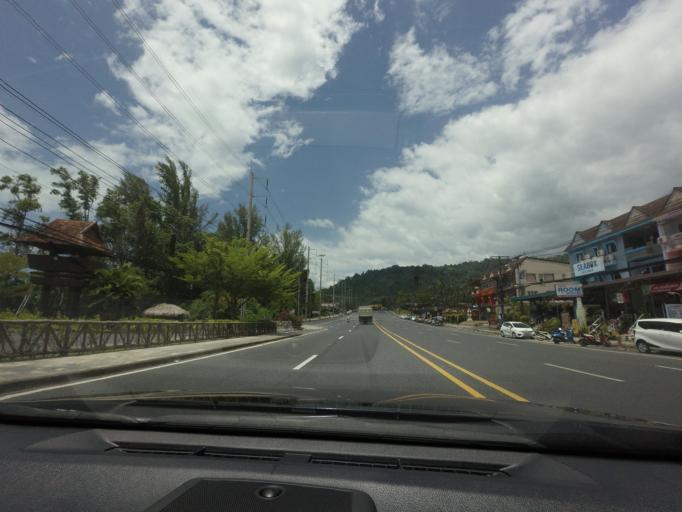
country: TH
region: Phangnga
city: Ban Khao Lak
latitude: 8.6389
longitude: 98.2491
